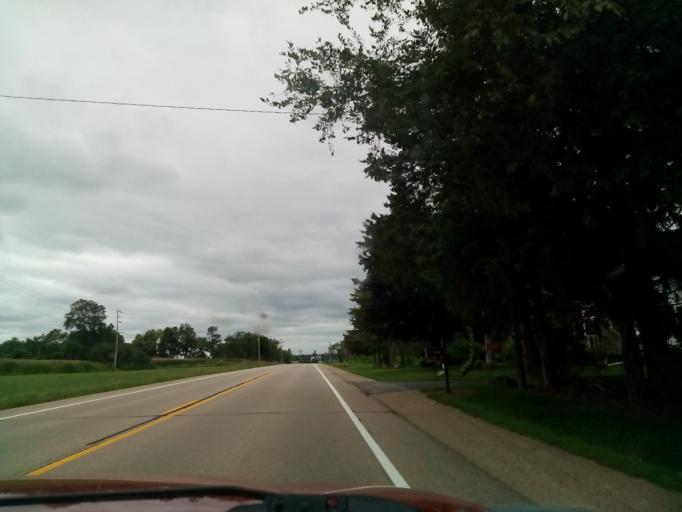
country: US
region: Wisconsin
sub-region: Waupaca County
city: New London
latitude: 44.2697
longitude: -88.7772
